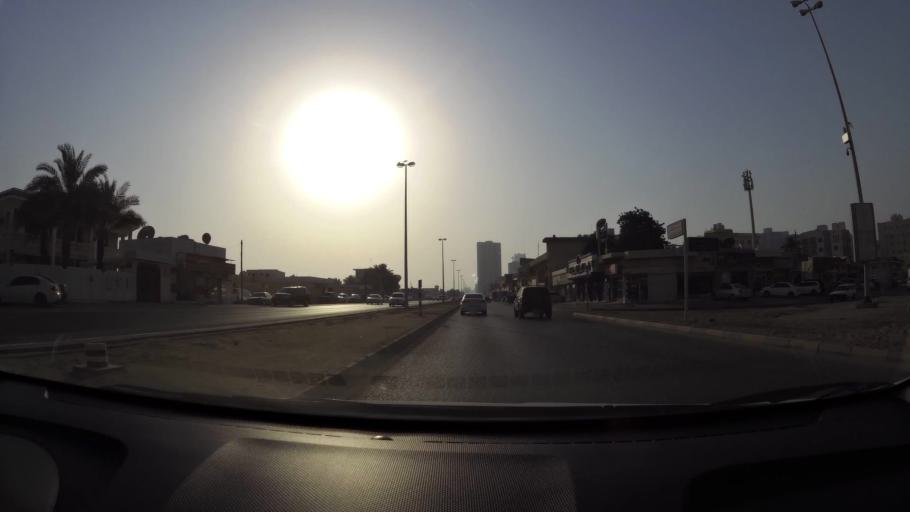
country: AE
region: Ajman
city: Ajman
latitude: 25.3834
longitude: 55.4449
